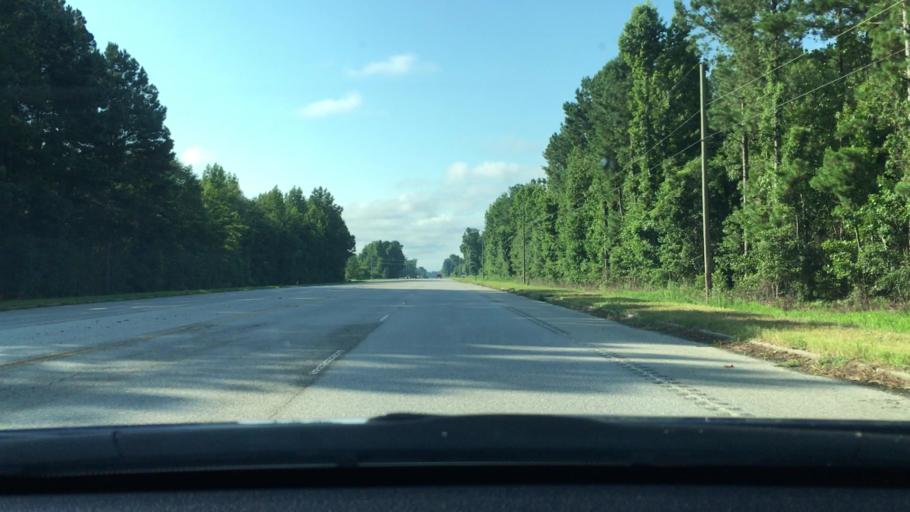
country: US
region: South Carolina
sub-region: Clarendon County
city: Manning
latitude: 33.7704
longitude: -80.2363
